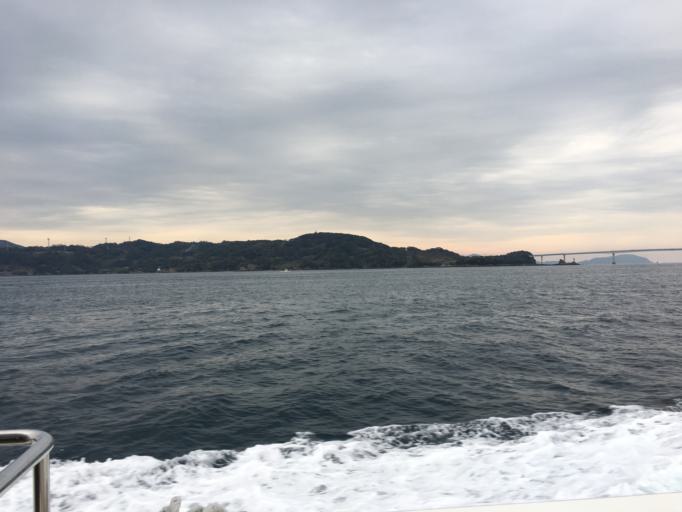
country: JP
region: Nagasaki
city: Nagasaki-shi
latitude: 32.7063
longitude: 129.7948
